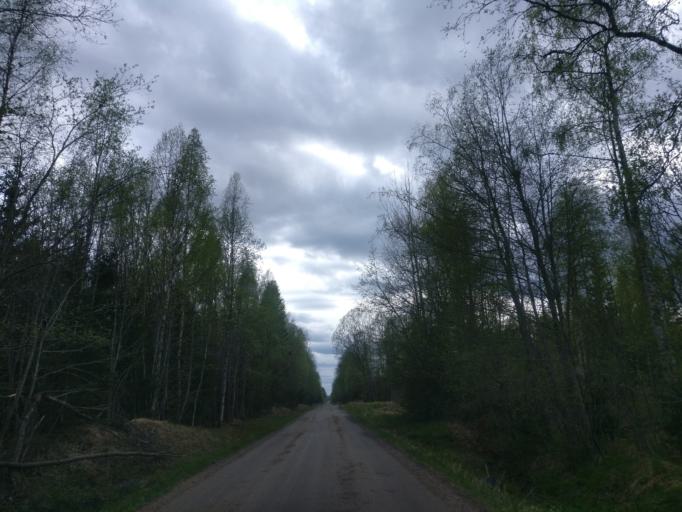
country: SE
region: Vaesternorrland
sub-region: Timra Kommun
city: Soraker
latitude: 62.5146
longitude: 17.5504
